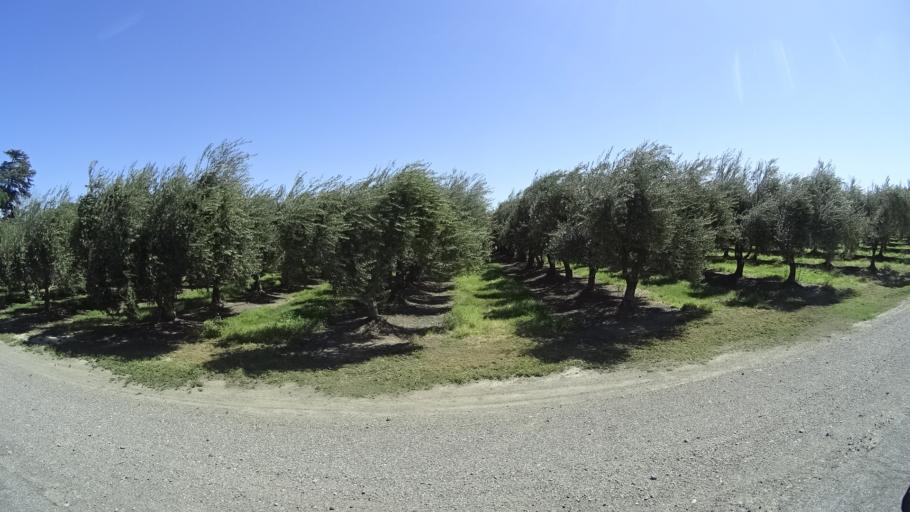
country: US
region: California
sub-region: Glenn County
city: Orland
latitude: 39.7092
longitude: -122.1456
